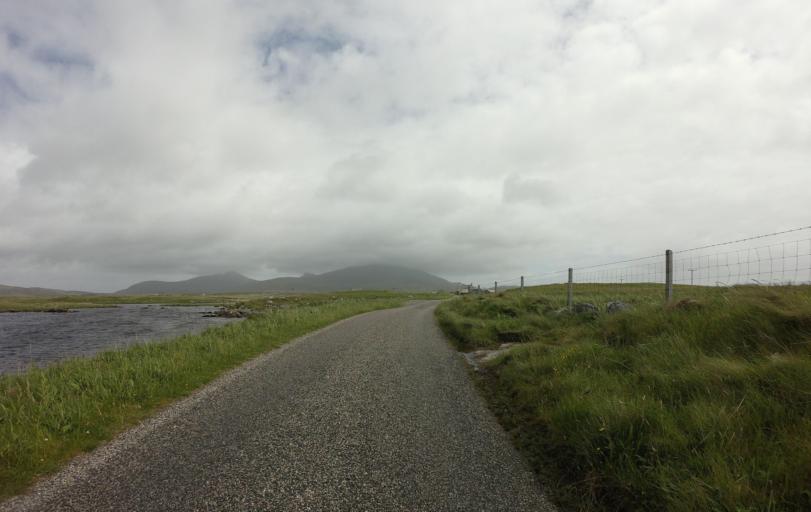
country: GB
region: Scotland
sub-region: Eilean Siar
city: Isle of South Uist
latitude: 57.2723
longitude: -7.4011
